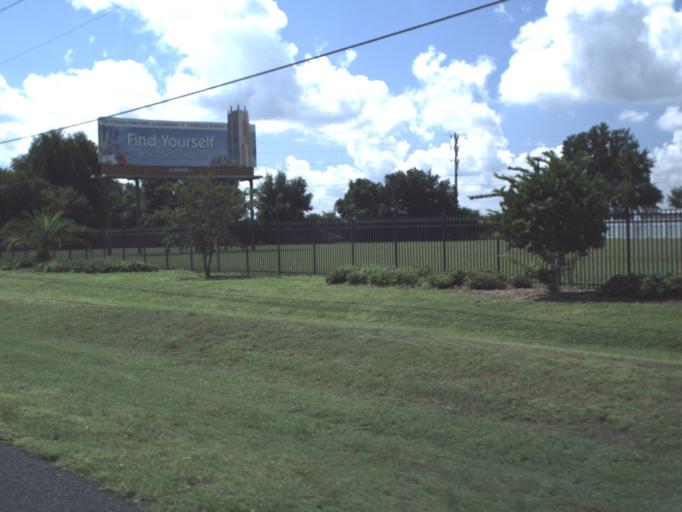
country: US
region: Florida
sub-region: Polk County
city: Lake Hamilton
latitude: 28.0655
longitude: -81.6408
